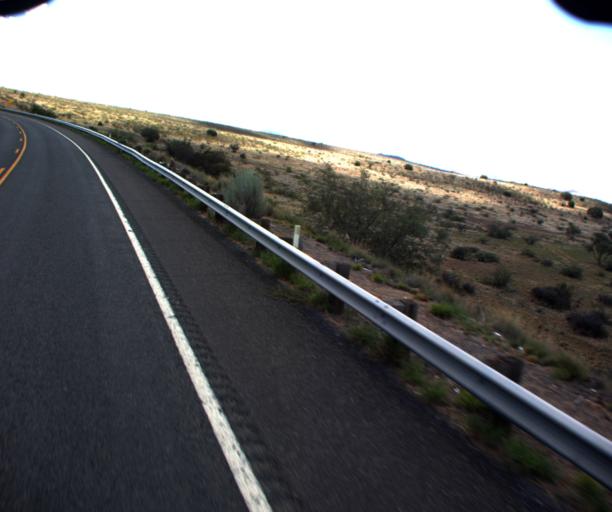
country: US
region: Arizona
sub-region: Yavapai County
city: Dewey-Humboldt
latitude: 34.5193
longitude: -112.0604
